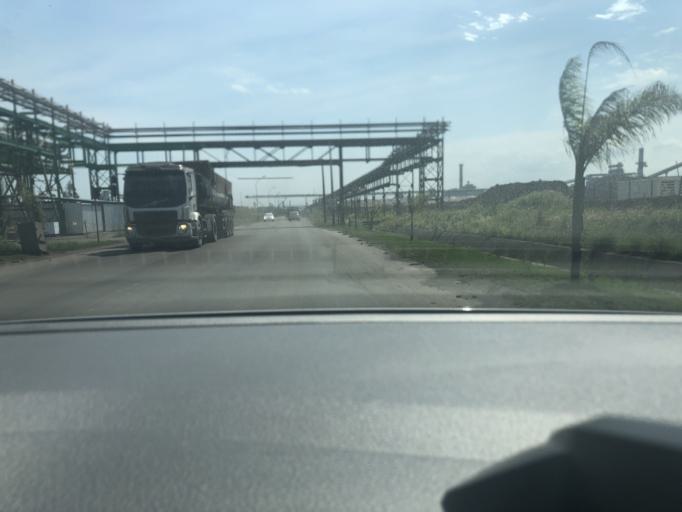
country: BR
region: Rio de Janeiro
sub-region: Itaguai
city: Itaguai
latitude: -22.9123
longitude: -43.7324
